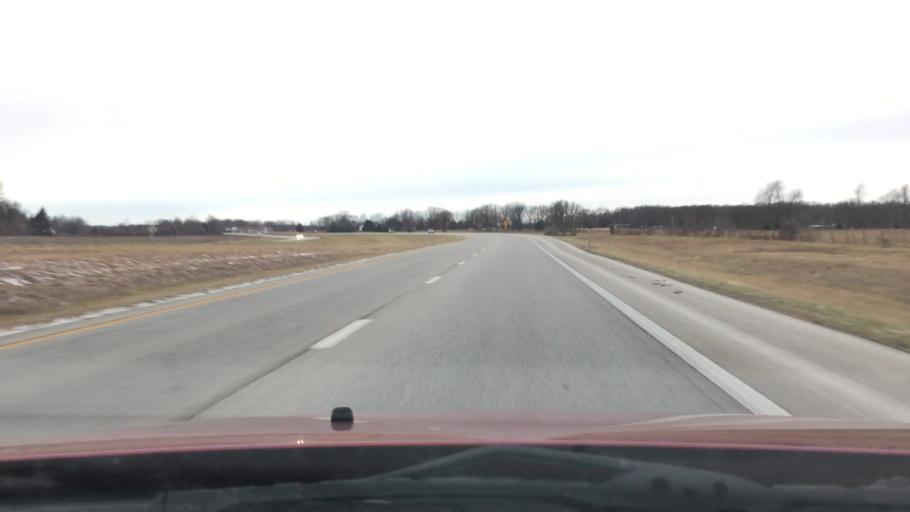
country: US
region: Missouri
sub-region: Webster County
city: Seymour
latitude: 37.1669
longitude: -92.8030
